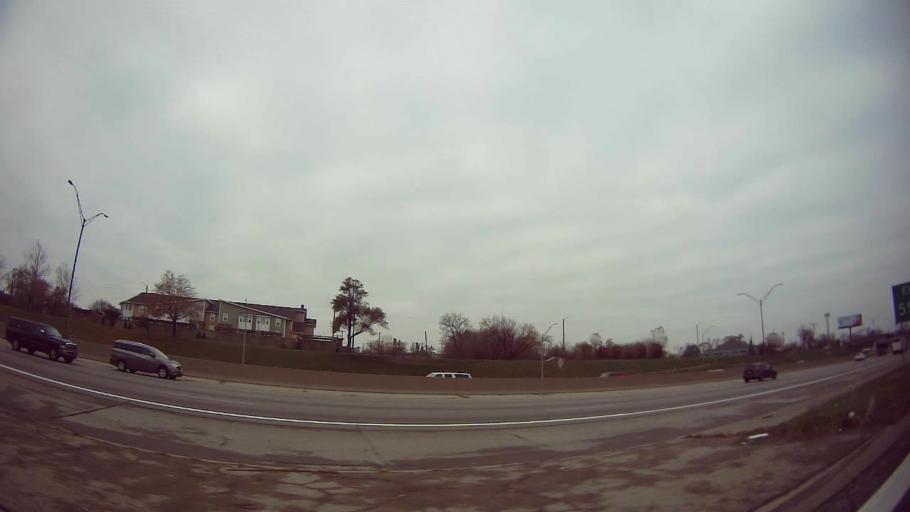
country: US
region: Michigan
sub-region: Wayne County
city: Hamtramck
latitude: 42.3846
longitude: -83.0665
